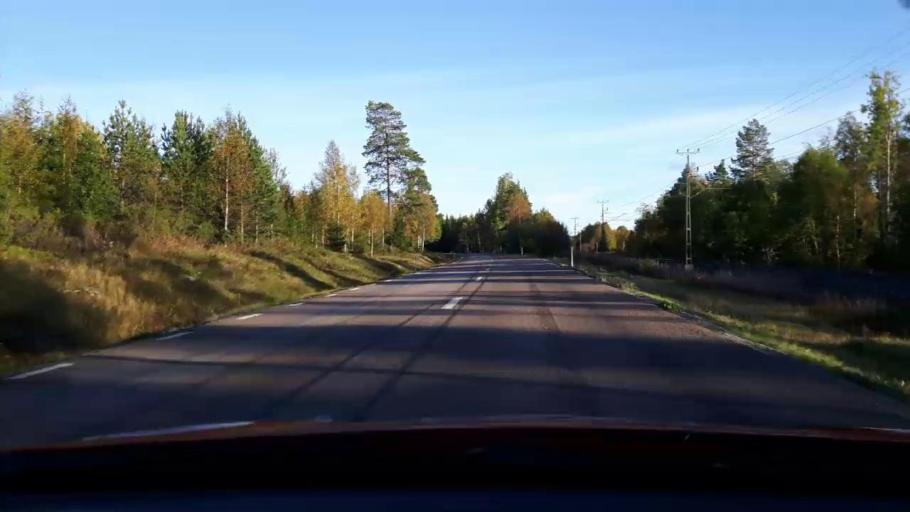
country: SE
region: Jaemtland
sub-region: OEstersunds Kommun
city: Brunflo
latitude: 63.0441
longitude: 14.8695
